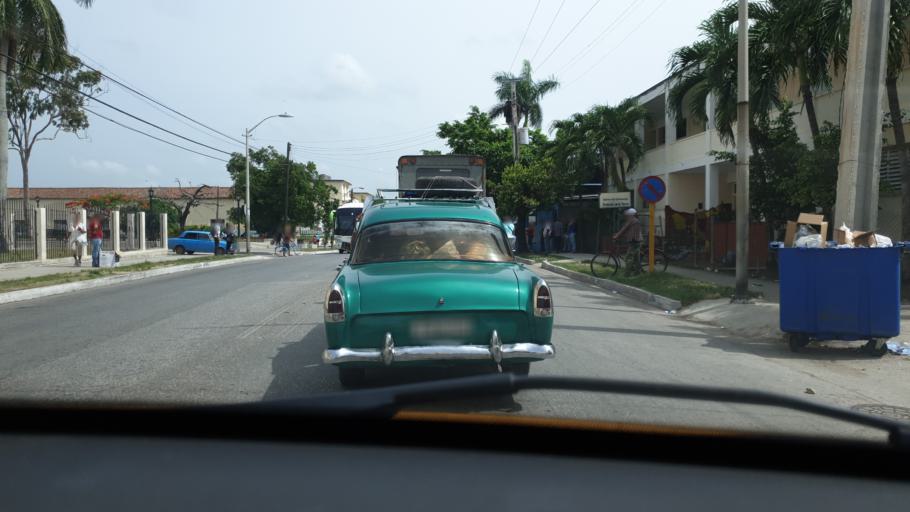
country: CU
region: Villa Clara
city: Santa Clara
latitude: 22.3993
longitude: -79.9637
